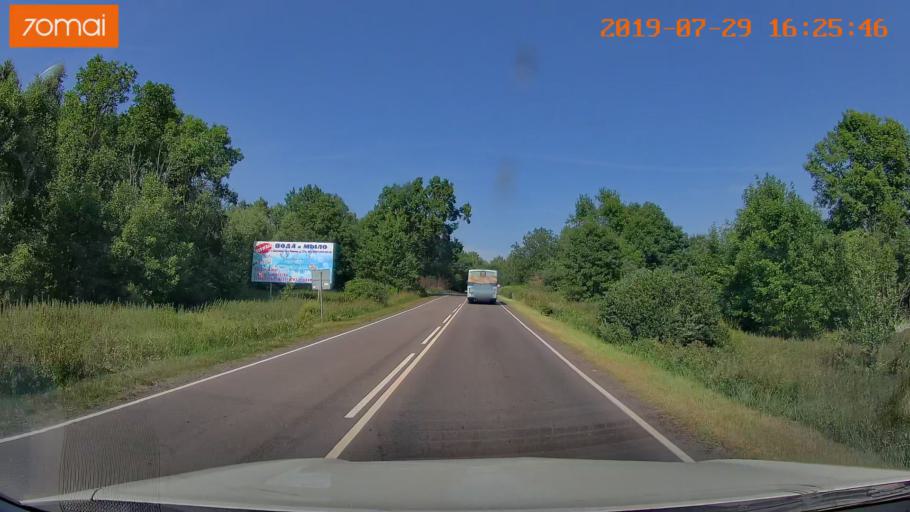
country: RU
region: Kaliningrad
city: Primorsk
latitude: 54.7253
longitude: 19.9693
